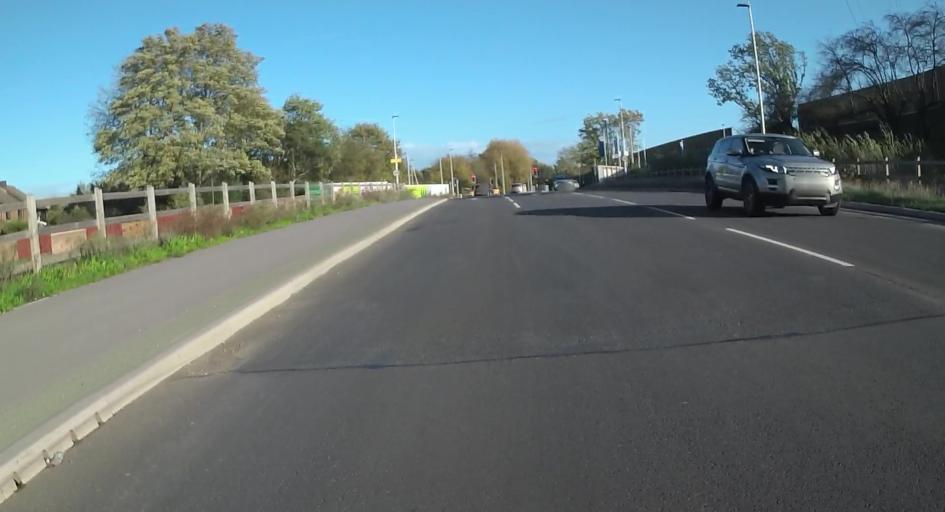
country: GB
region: England
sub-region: Wokingham
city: Winnersh
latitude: 51.4252
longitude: -0.8830
